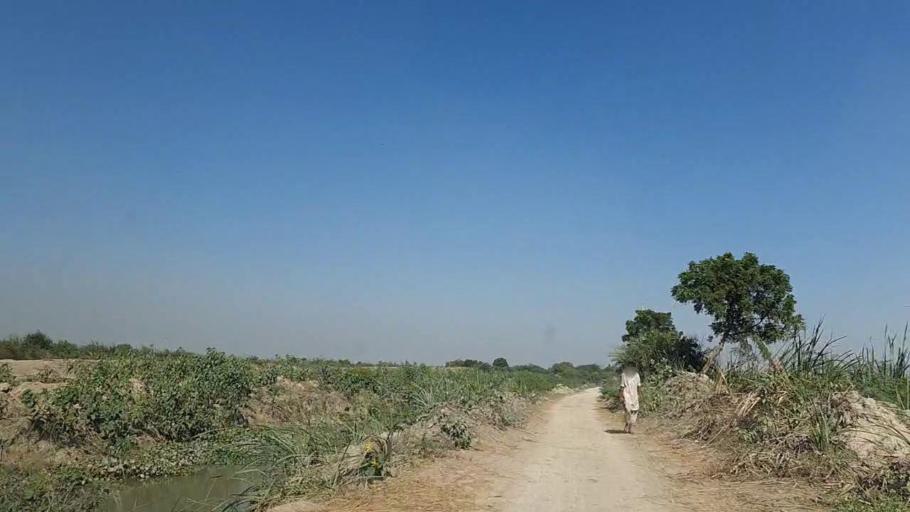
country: PK
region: Sindh
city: Daro Mehar
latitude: 24.7701
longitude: 68.1555
